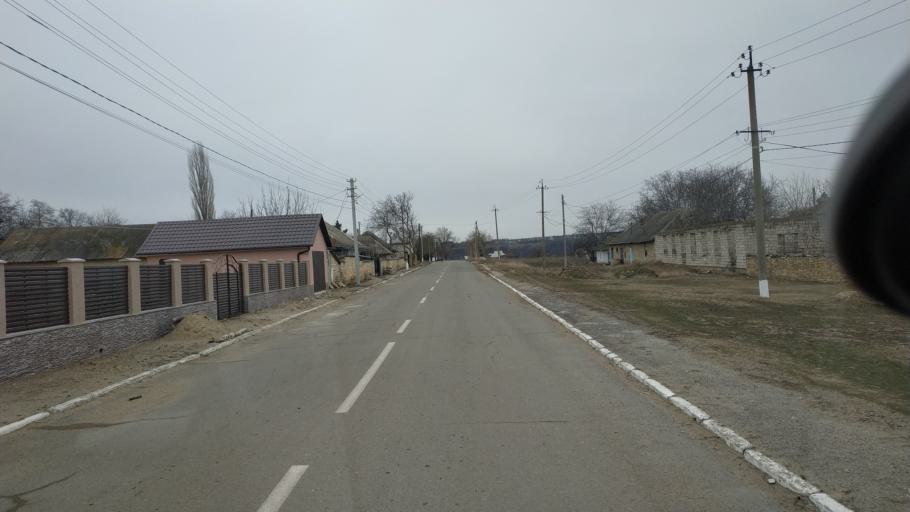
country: MD
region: Telenesti
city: Cocieri
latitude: 47.3411
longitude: 29.1191
